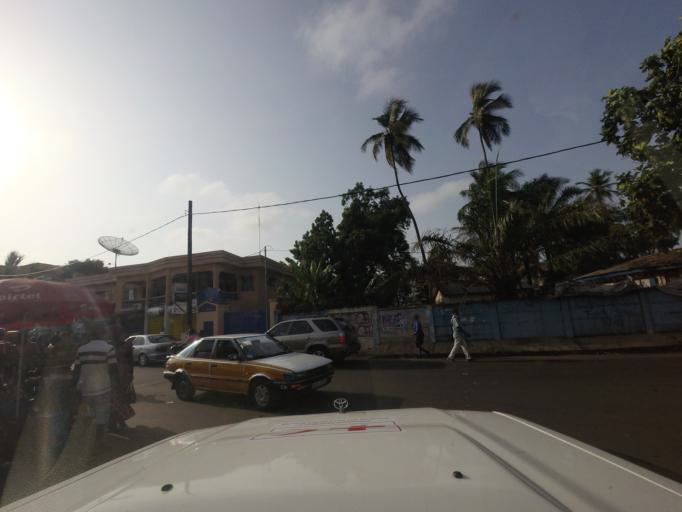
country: SL
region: Western Area
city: Freetown
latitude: 8.4850
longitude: -13.2662
